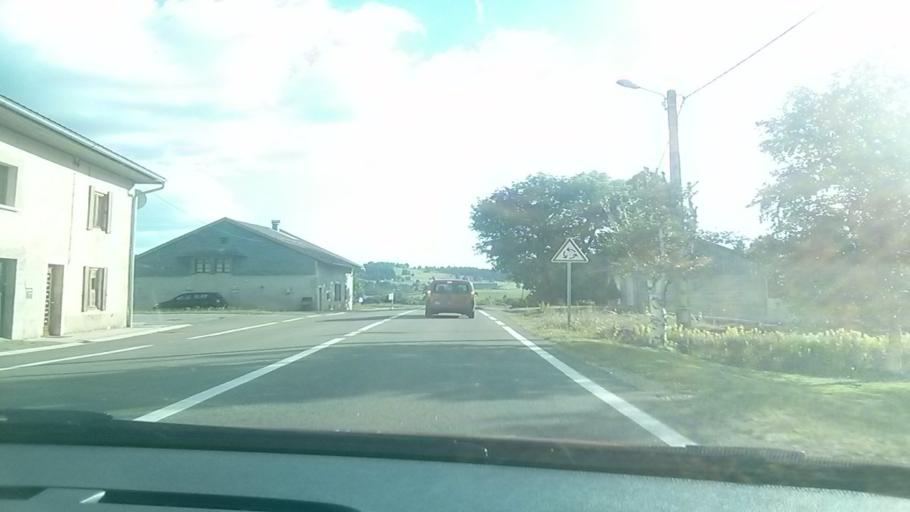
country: FR
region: Franche-Comte
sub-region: Departement du Jura
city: Les Rousses
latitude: 46.4921
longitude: 6.0928
